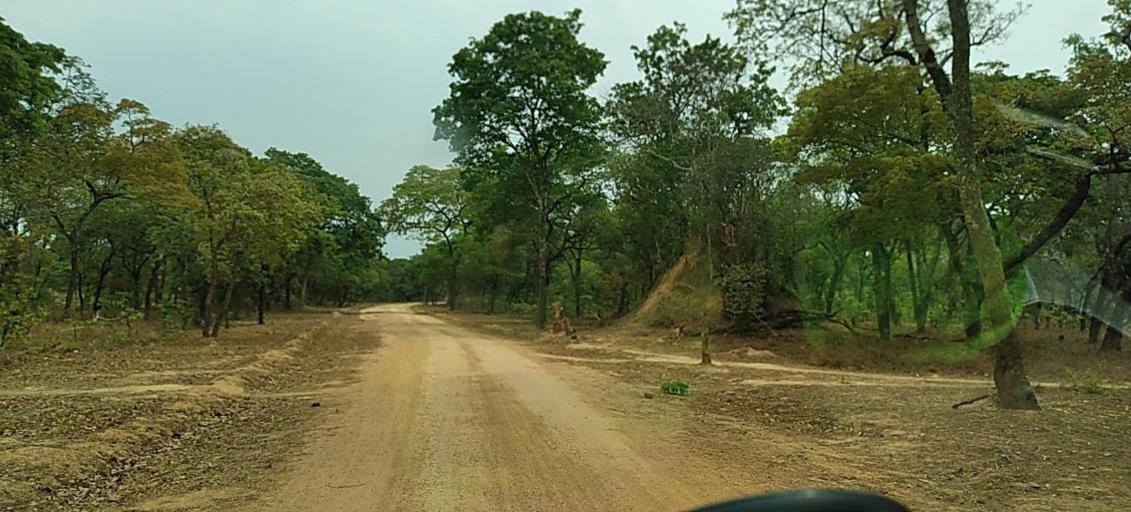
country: ZM
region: North-Western
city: Solwezi
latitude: -12.9296
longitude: 26.5604
